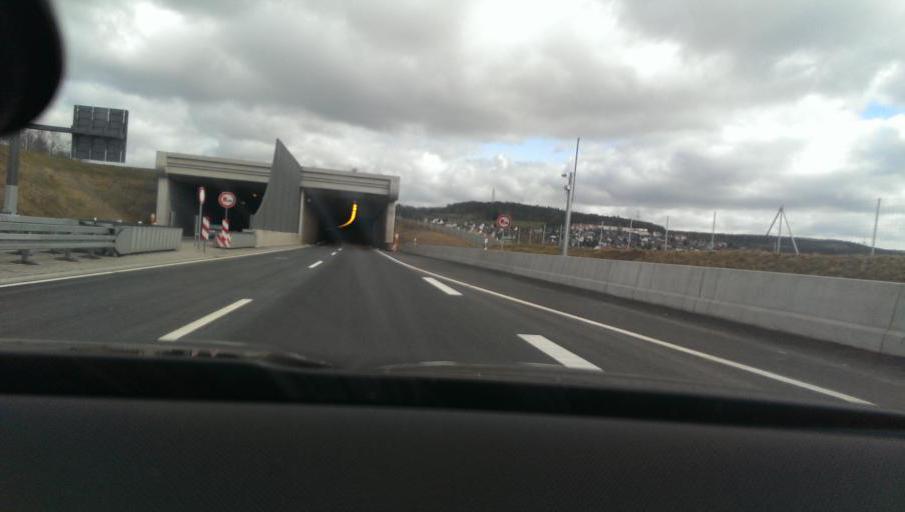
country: DE
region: Hesse
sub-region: Regierungsbezirk Kassel
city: Neuhof
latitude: 50.4443
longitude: 9.6108
